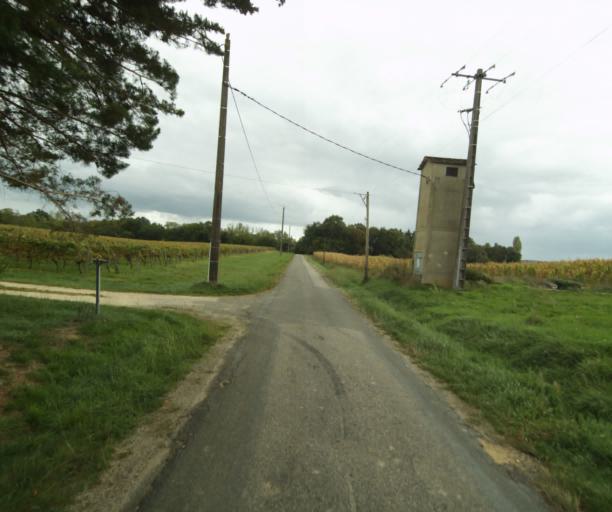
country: FR
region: Midi-Pyrenees
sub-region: Departement du Gers
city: Eauze
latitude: 43.8882
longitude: 0.1072
